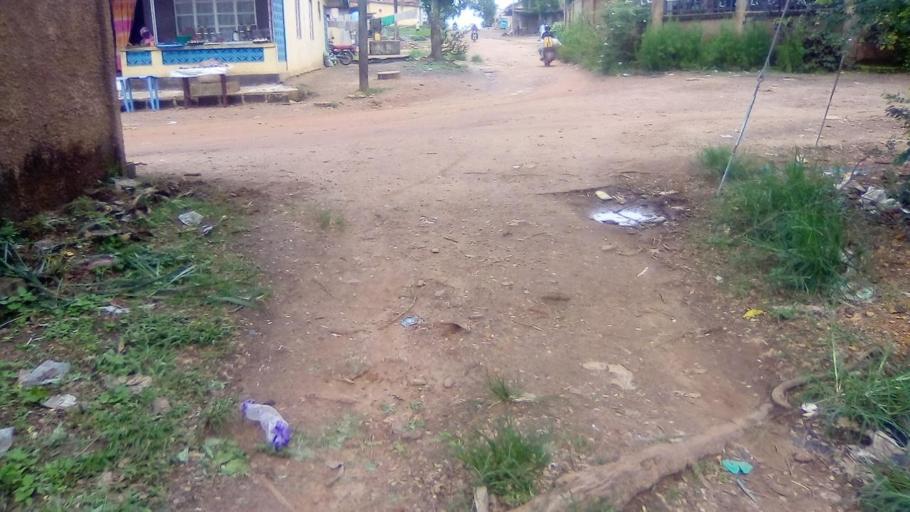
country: SL
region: Southern Province
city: Bo
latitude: 7.9434
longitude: -11.7414
